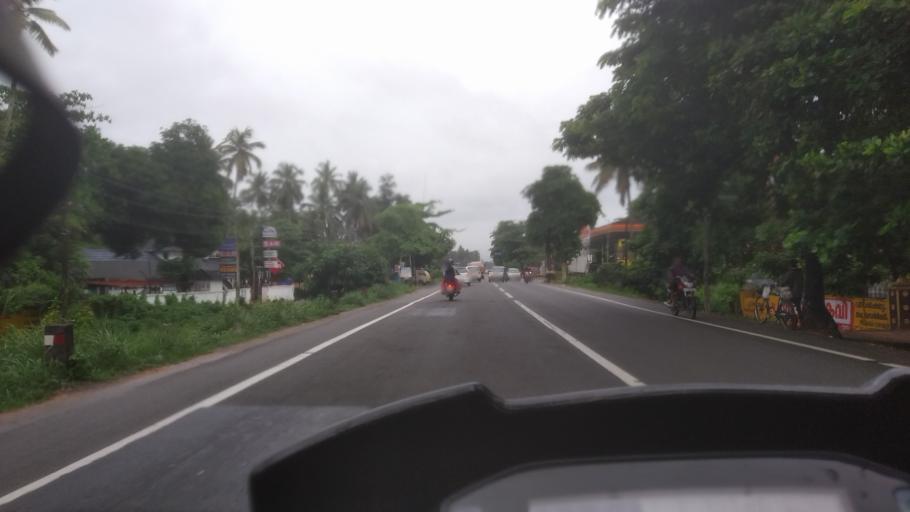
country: IN
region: Kerala
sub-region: Alappuzha
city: Kayankulam
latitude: 9.1639
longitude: 76.5033
